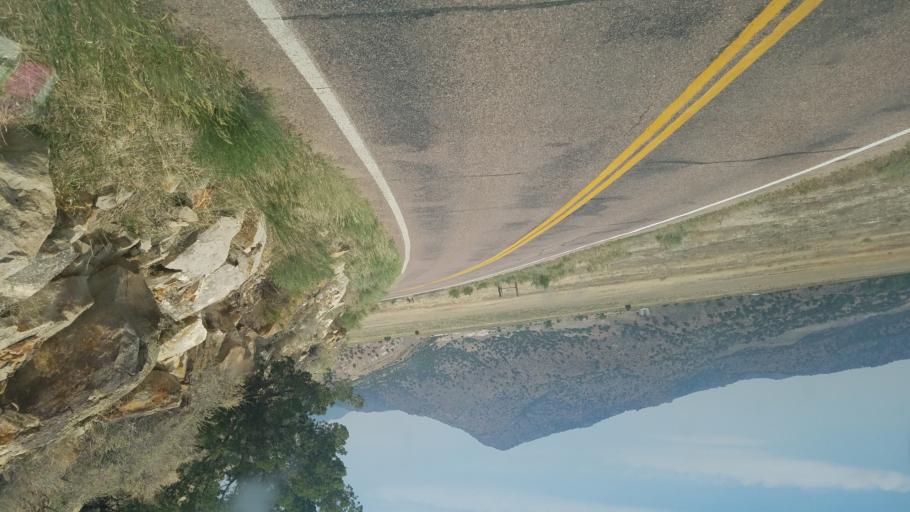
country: US
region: Colorado
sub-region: Fremont County
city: Canon City
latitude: 38.4802
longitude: -105.3801
